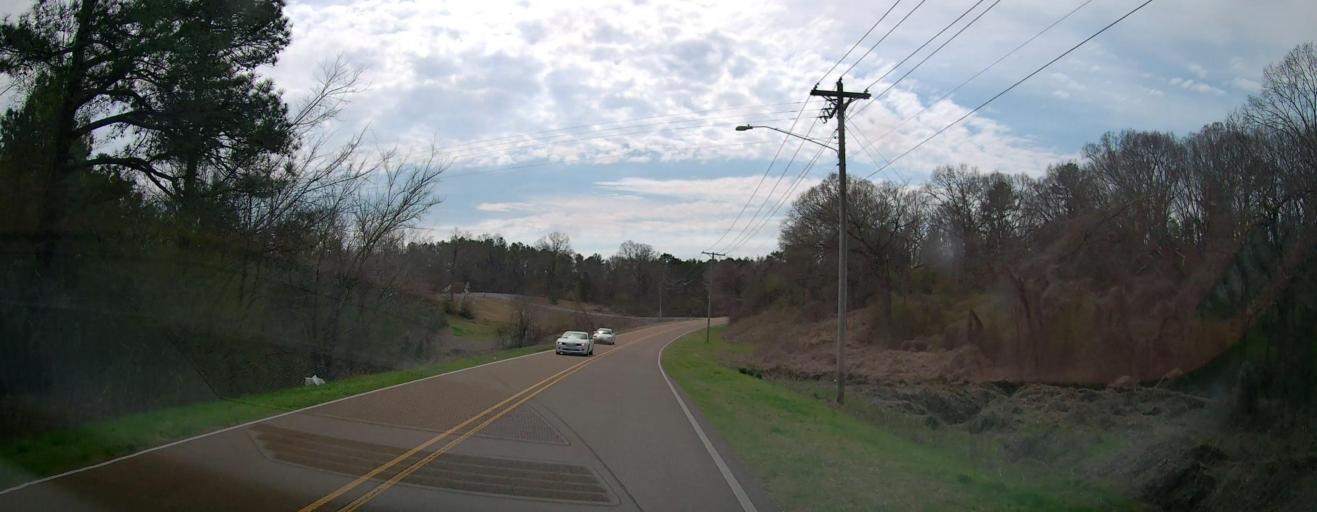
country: US
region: Mississippi
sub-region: Marshall County
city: Holly Springs
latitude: 34.7591
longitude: -89.4296
